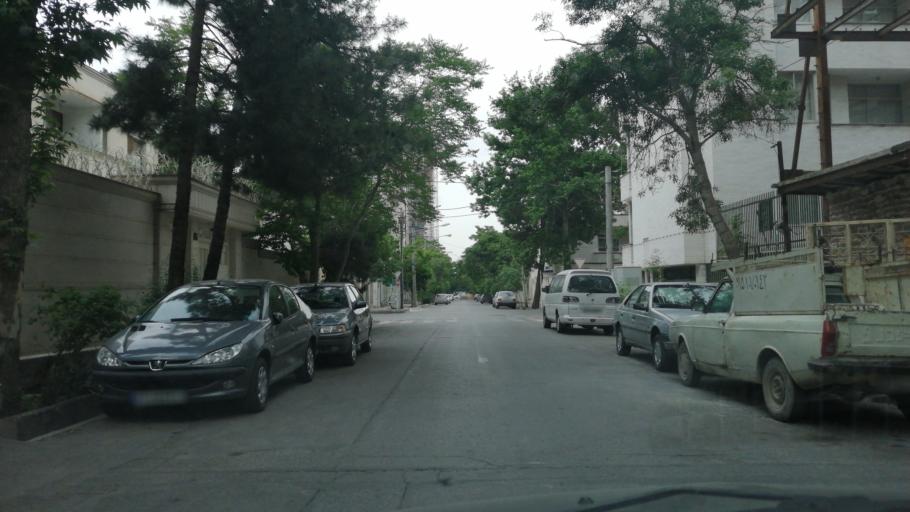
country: IR
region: Razavi Khorasan
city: Mashhad
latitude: 36.2852
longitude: 59.5724
